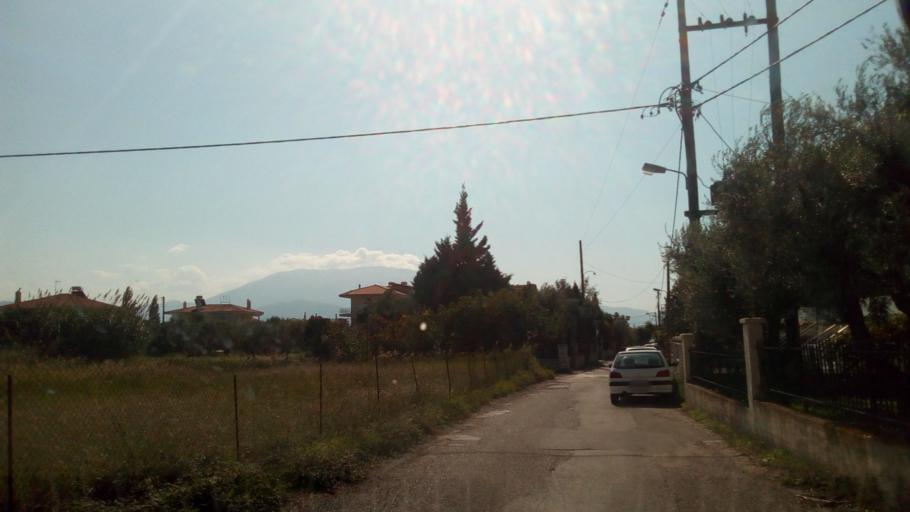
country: GR
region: West Greece
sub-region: Nomos Aitolias kai Akarnanias
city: Nafpaktos
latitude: 38.3767
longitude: 21.7943
